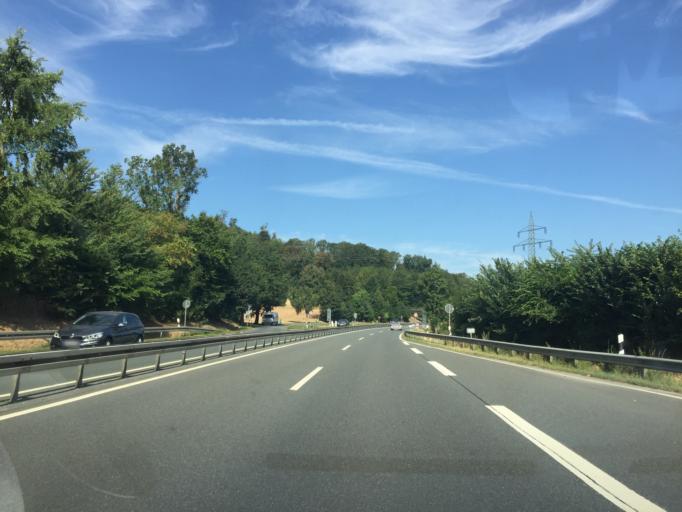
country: DE
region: Lower Saxony
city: Gittelde
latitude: 51.8313
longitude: 10.1895
